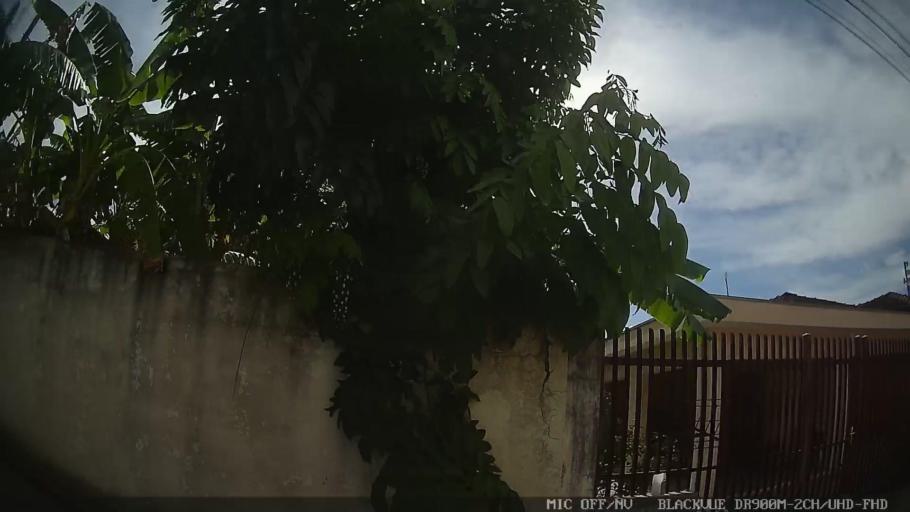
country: BR
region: Sao Paulo
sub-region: Conchas
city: Conchas
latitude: -23.0687
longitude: -47.9772
